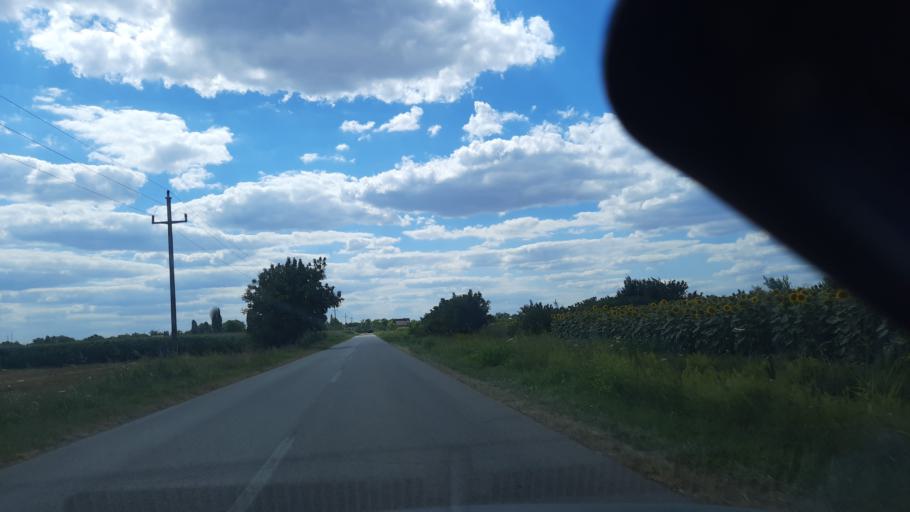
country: RS
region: Autonomna Pokrajina Vojvodina
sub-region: Sremski Okrug
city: Pecinci
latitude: 44.9066
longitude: 19.9427
